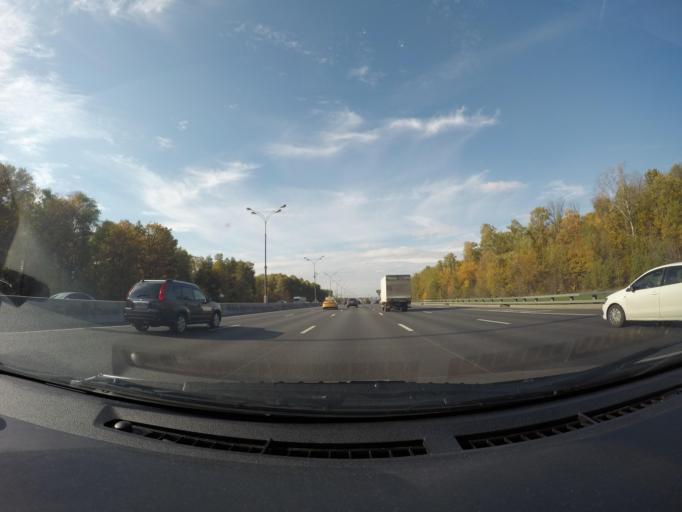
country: RU
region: Moscow
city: Vatutino
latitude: 55.8961
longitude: 37.6558
